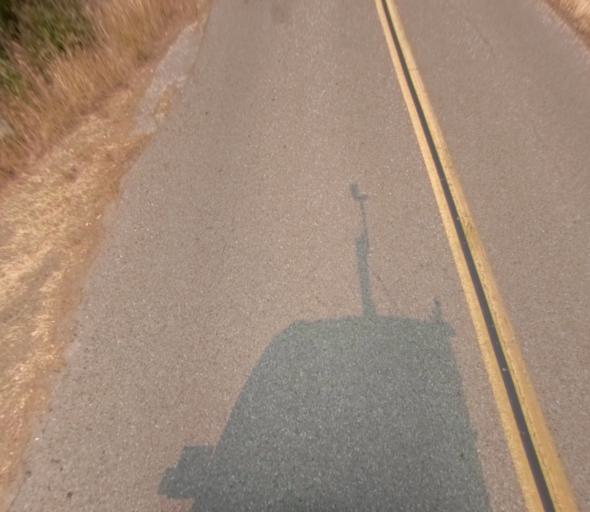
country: US
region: California
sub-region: Madera County
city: Oakhurst
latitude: 37.3154
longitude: -119.6174
